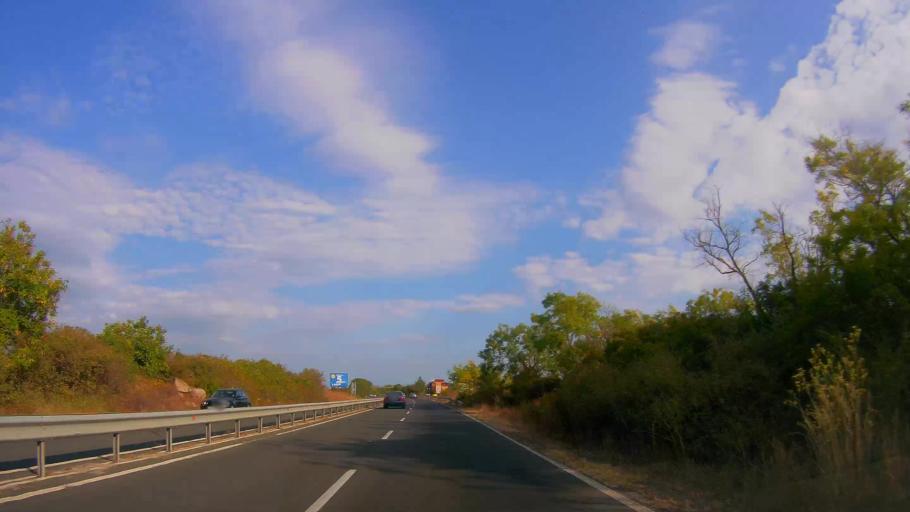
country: BG
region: Burgas
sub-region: Obshtina Sozopol
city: Chernomorets
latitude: 42.4293
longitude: 27.6398
